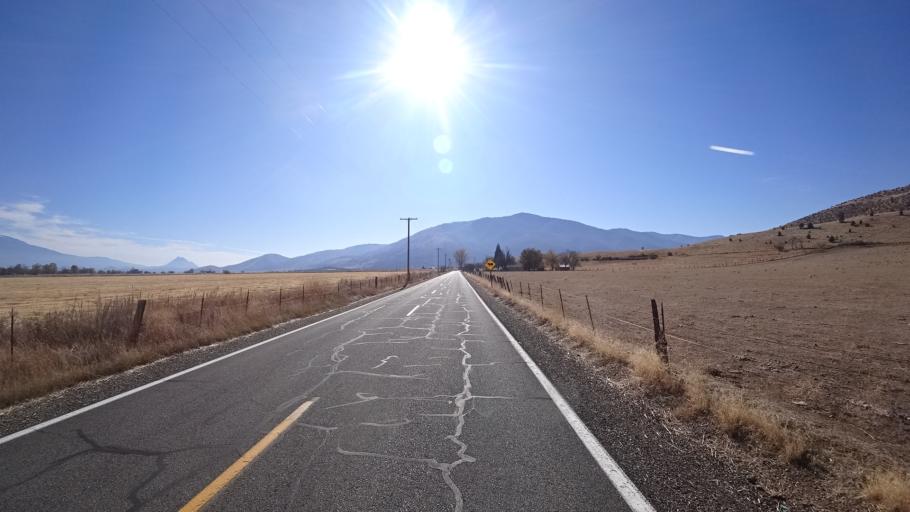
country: US
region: California
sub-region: Siskiyou County
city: Weed
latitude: 41.5170
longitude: -122.5256
